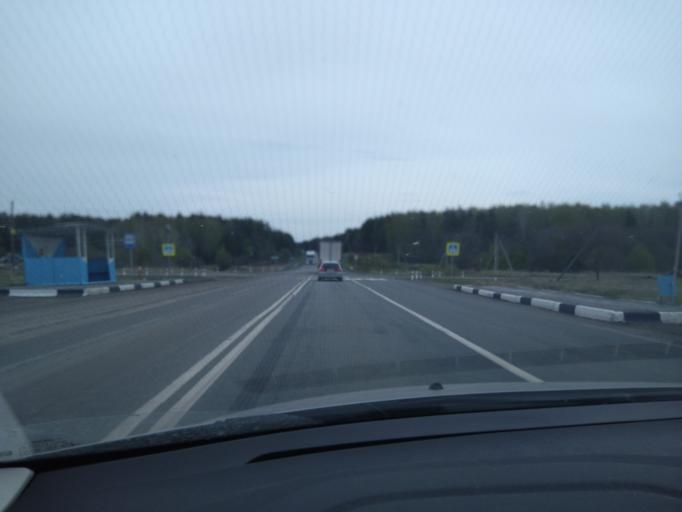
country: RU
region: Sverdlovsk
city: Pyshma
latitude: 57.0461
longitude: 63.4654
